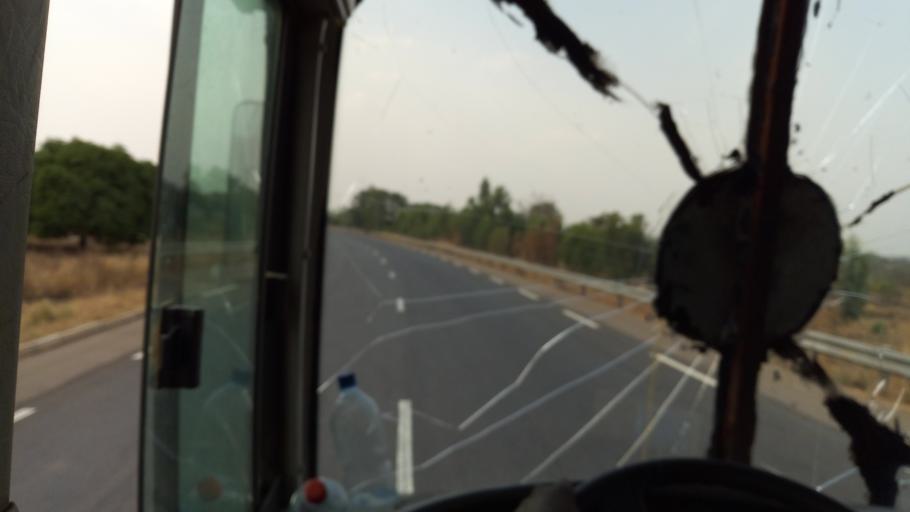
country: TG
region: Kara
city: Bafilo
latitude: 9.3601
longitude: 1.2549
